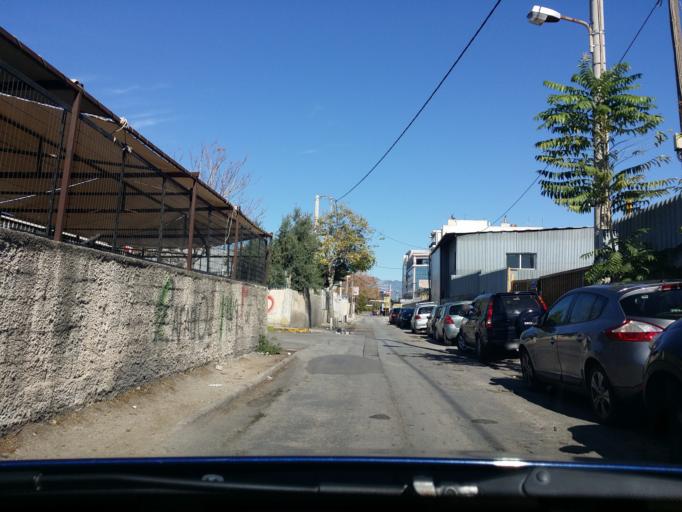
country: GR
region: Attica
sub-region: Nomarchia Athinas
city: Peristeri
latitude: 37.9970
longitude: 23.7006
